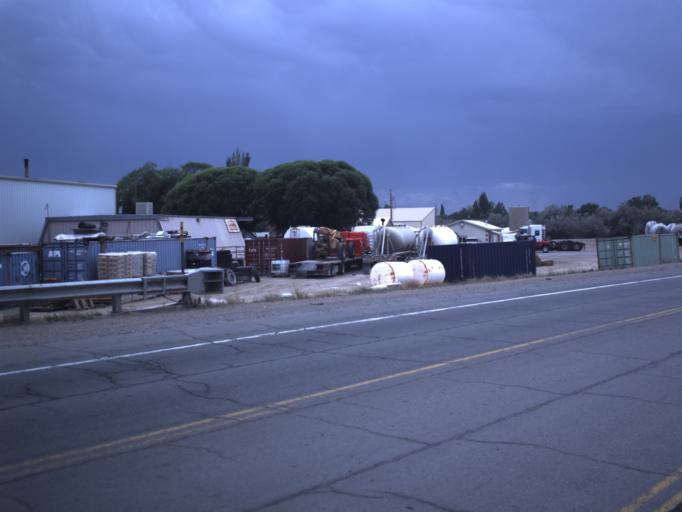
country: US
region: Utah
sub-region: Duchesne County
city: Roosevelt
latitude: 40.1988
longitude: -110.0681
